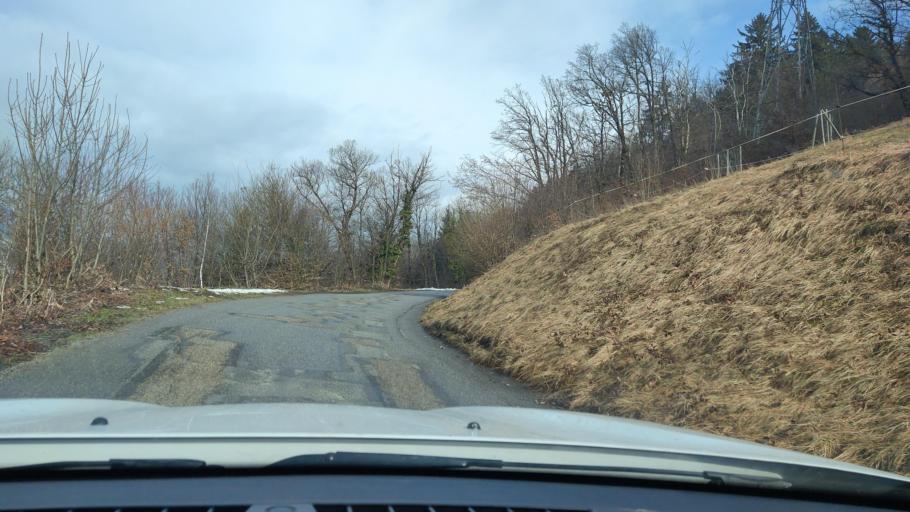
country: FR
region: Rhone-Alpes
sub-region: Departement de la Savoie
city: Marthod
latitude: 45.6964
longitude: 6.4139
